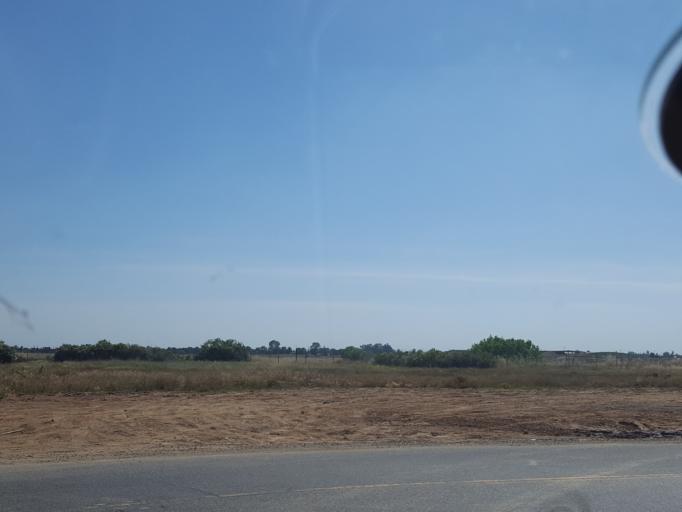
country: US
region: California
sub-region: Sacramento County
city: La Riviera
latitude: 38.5416
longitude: -121.3212
